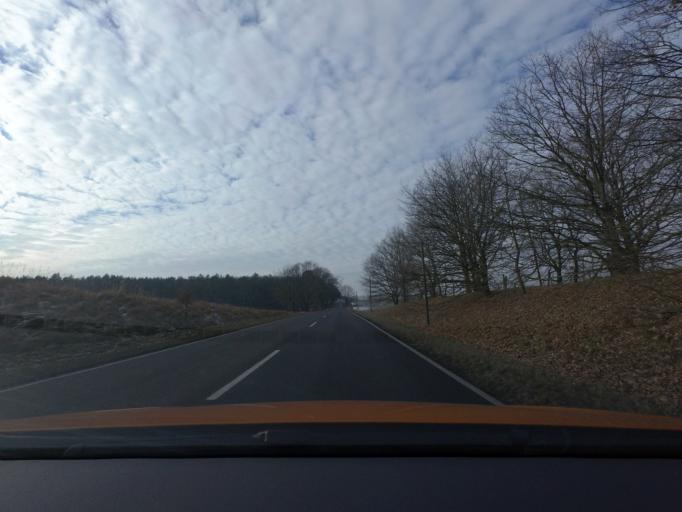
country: DE
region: Brandenburg
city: Zehdenick
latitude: 52.8995
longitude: 13.2302
